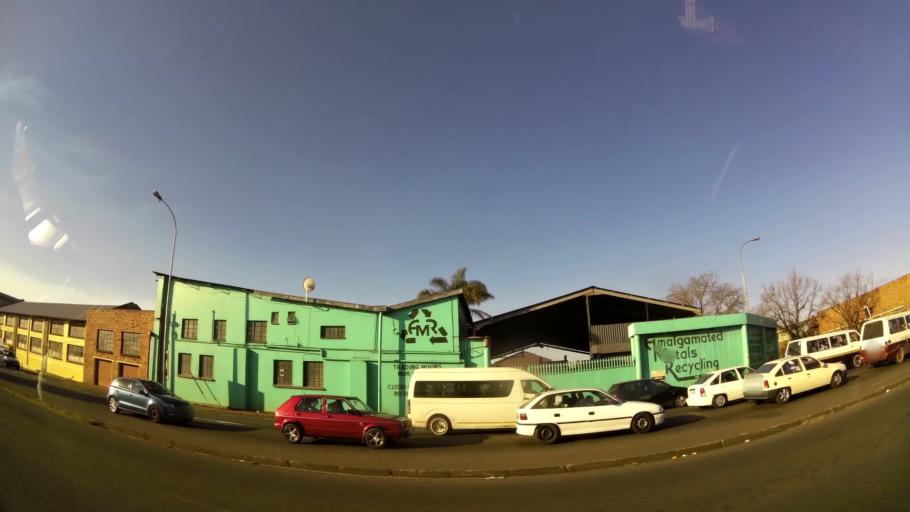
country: ZA
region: Gauteng
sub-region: City of Johannesburg Metropolitan Municipality
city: Roodepoort
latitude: -26.1528
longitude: 27.8654
